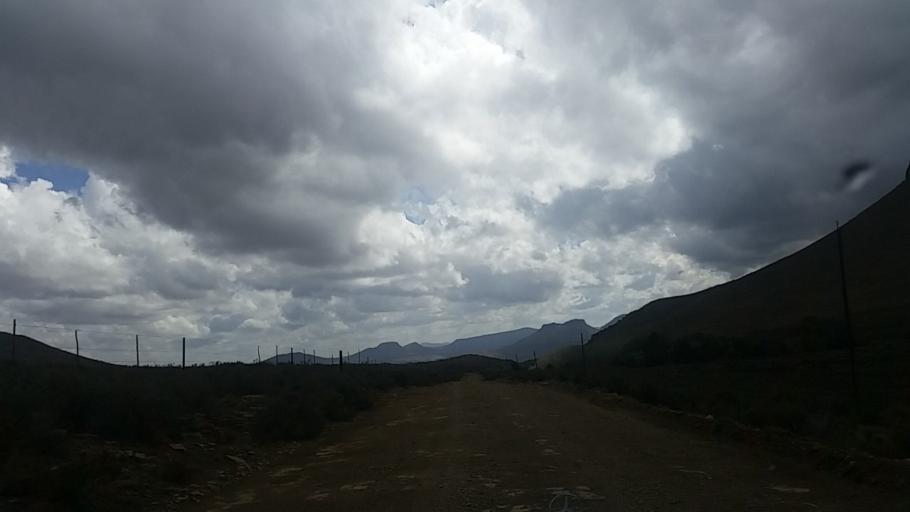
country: ZA
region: Eastern Cape
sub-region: Chris Hani District Municipality
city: Middelburg
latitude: -31.7900
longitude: 24.6683
